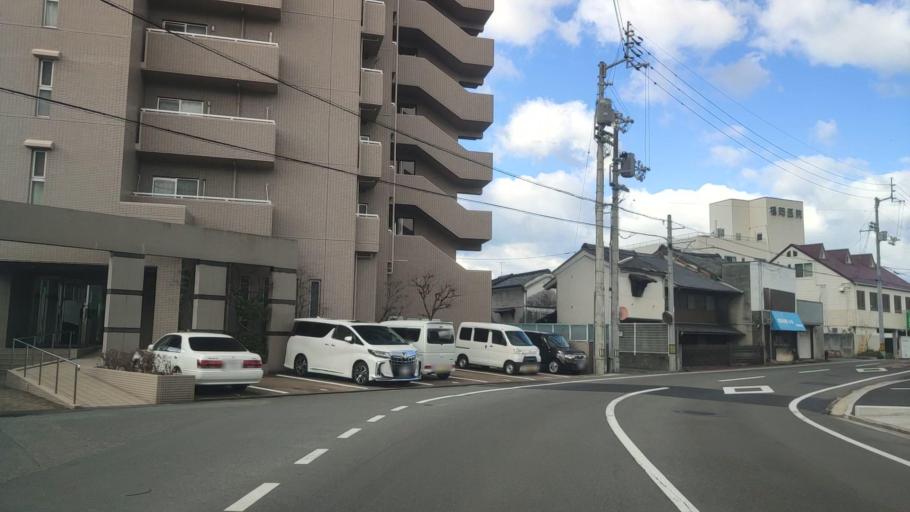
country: JP
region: Ehime
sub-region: Shikoku-chuo Shi
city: Matsuyama
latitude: 33.8647
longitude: 132.7141
